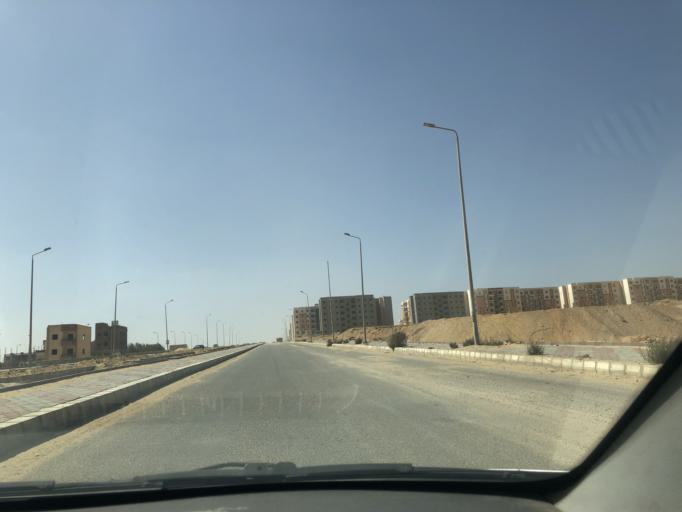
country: EG
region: Al Jizah
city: Madinat Sittah Uktubar
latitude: 29.9324
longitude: 31.0100
